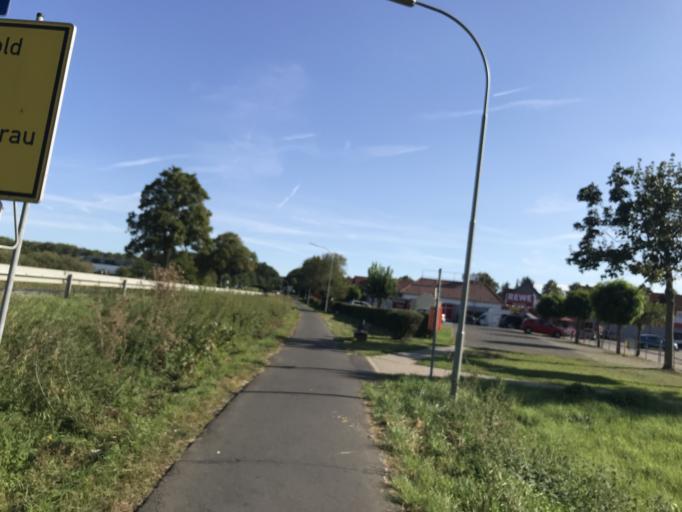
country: DE
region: Hesse
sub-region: Regierungsbezirk Darmstadt
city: Altenstadt
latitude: 50.2770
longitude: 8.9481
